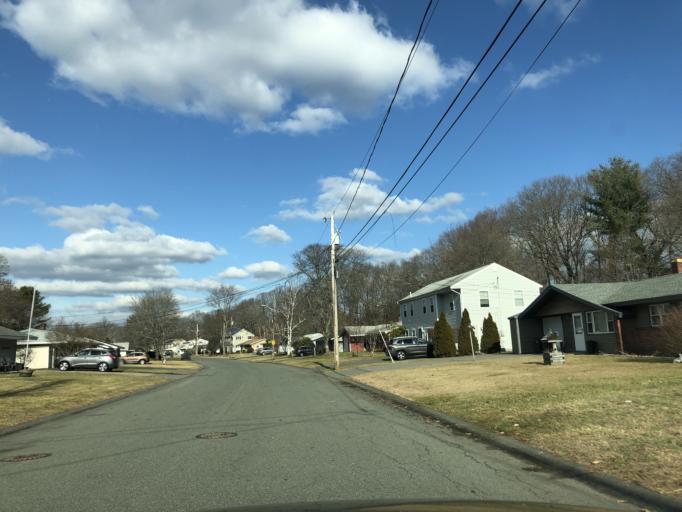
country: US
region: Massachusetts
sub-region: Plymouth County
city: Brockton
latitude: 42.1130
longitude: -71.0027
